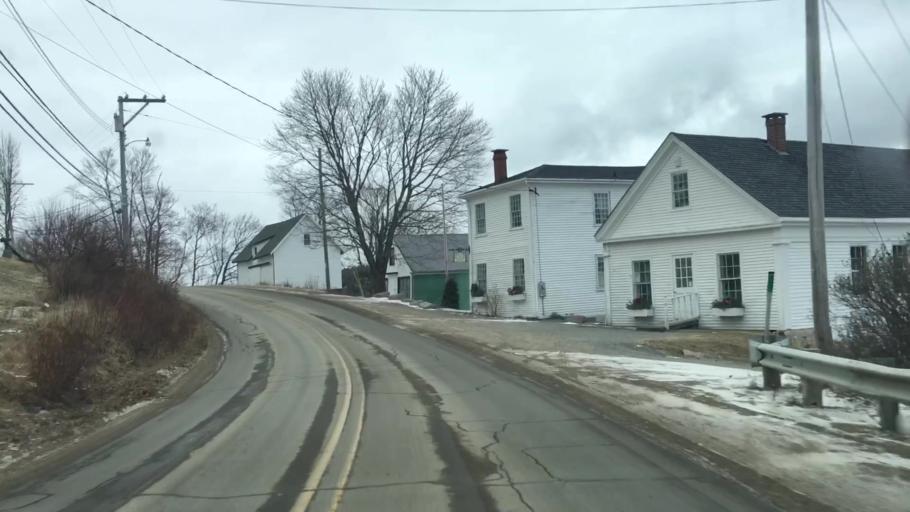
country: US
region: Maine
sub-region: Washington County
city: Machiasport
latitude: 44.6968
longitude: -67.3939
